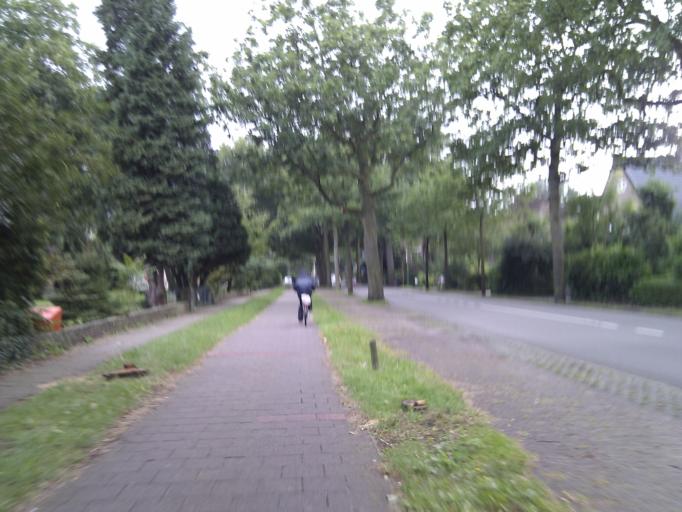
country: NL
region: Utrecht
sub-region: Gemeente De Bilt
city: De Bilt
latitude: 52.1238
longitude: 5.2004
